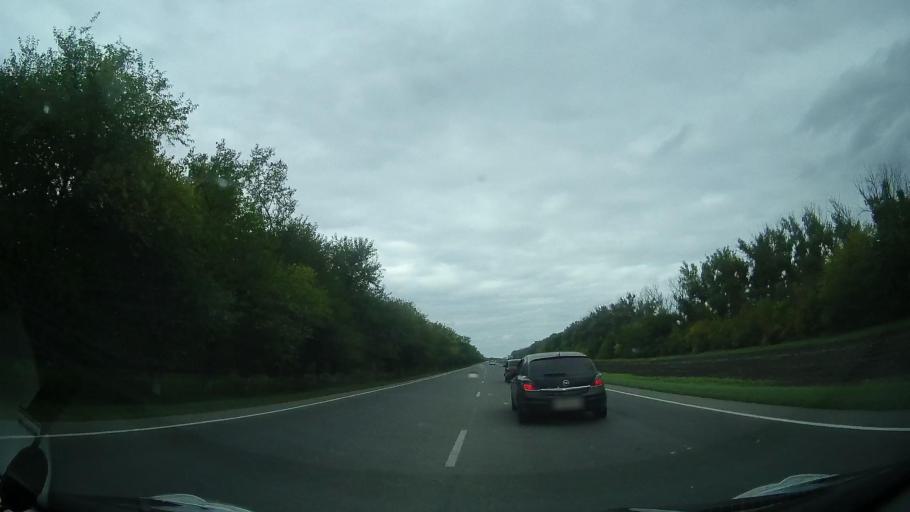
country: RU
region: Rostov
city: Yegorlykskaya
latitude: 46.6077
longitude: 40.6108
